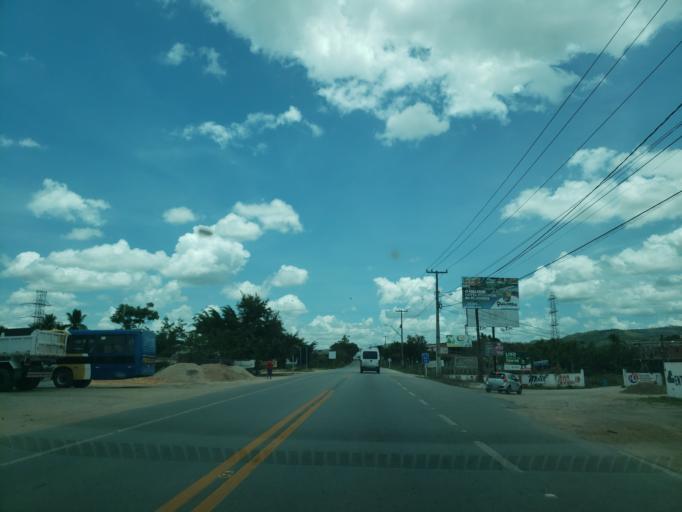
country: BR
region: Alagoas
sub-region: Uniao Dos Palmares
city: Uniao dos Palmares
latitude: -9.1613
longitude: -36.0167
